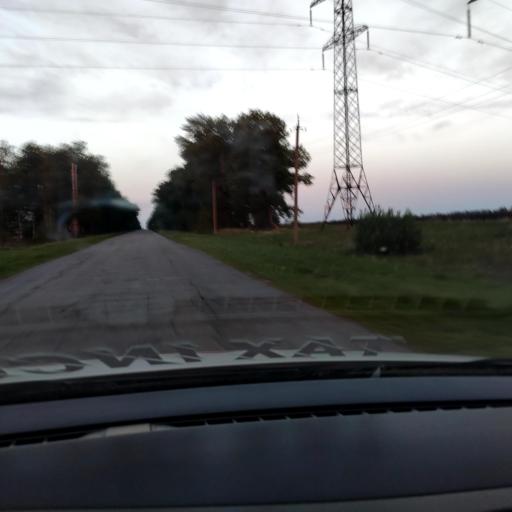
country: RU
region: Voronezj
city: Maslovka
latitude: 51.4418
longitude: 39.2735
